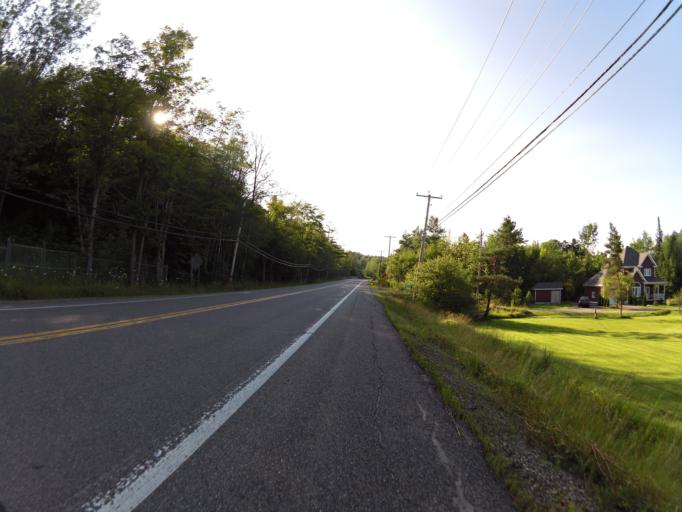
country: CA
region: Quebec
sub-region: Outaouais
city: Wakefield
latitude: 45.5428
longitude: -75.8189
